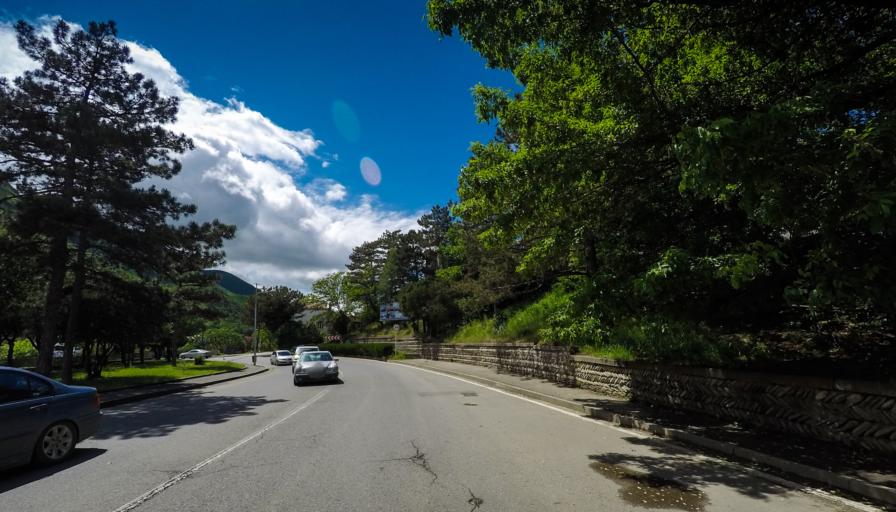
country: GE
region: Mtskheta-Mtianeti
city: Mtskheta
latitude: 41.8399
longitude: 44.7050
